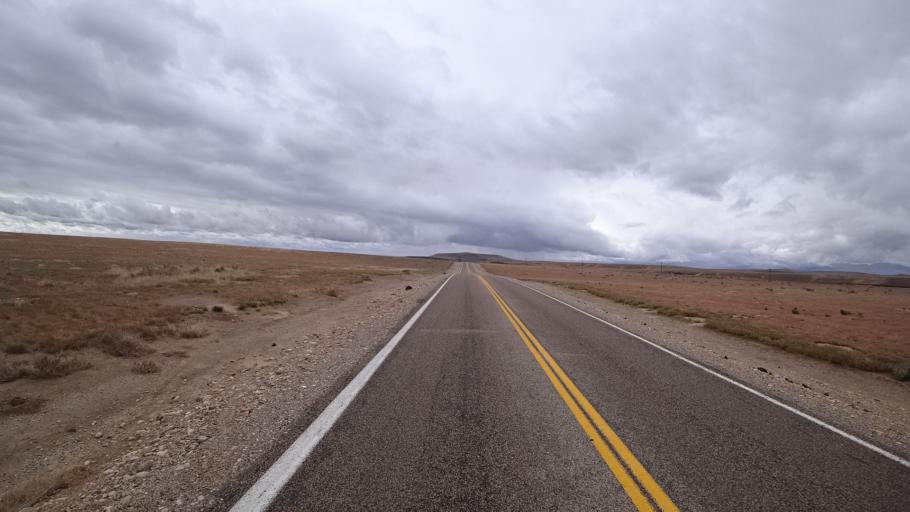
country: US
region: Idaho
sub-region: Owyhee County
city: Murphy
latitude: 43.2822
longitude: -116.3943
